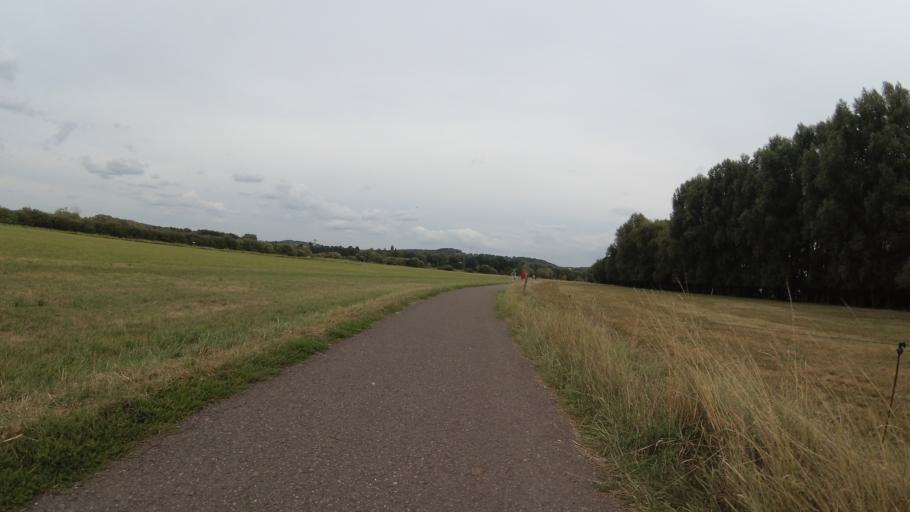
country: DE
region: Saarland
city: Homburg
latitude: 49.3095
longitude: 7.2964
